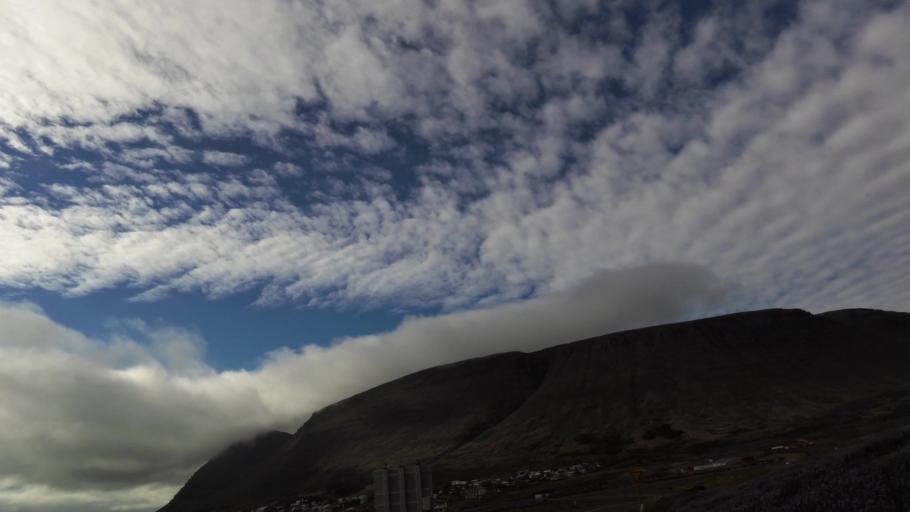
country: IS
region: West
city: Olafsvik
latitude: 65.5871
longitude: -23.9701
